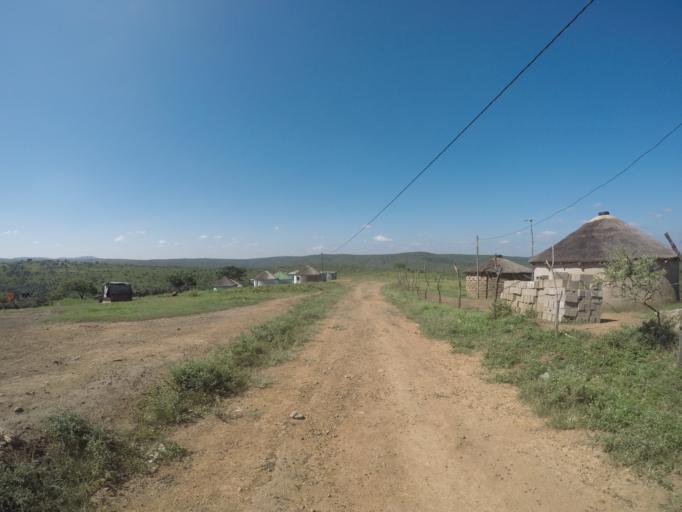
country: ZA
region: KwaZulu-Natal
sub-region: uThungulu District Municipality
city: Empangeni
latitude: -28.5566
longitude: 31.7057
